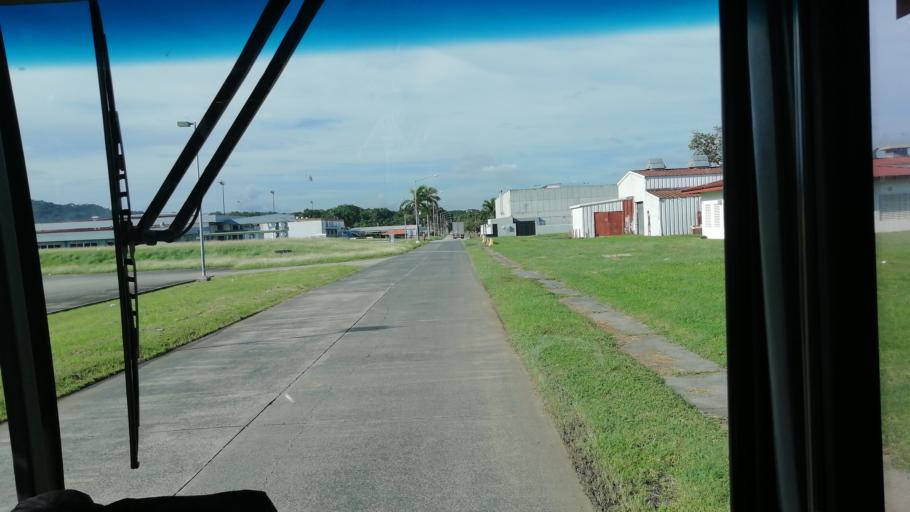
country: PA
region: Panama
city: Veracruz
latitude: 8.9182
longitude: -79.5944
